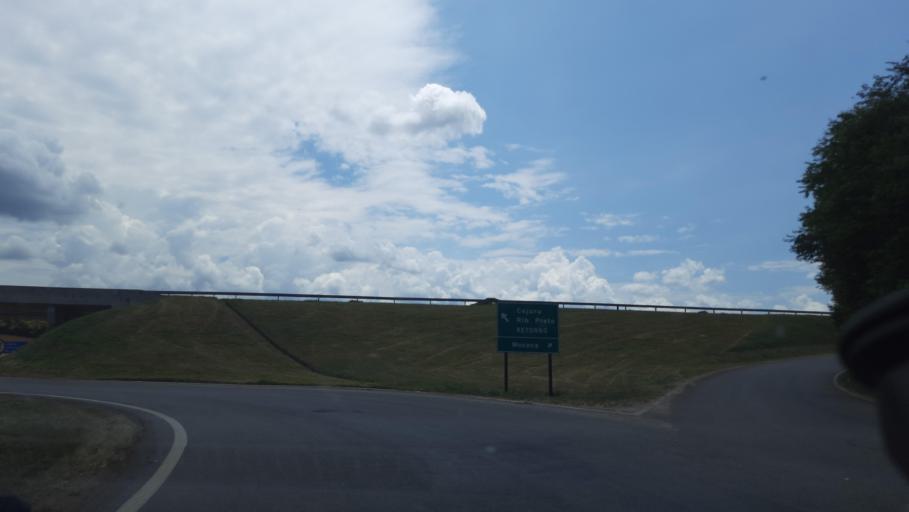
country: BR
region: Sao Paulo
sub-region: Mococa
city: Mococa
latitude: -21.5202
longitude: -47.0260
